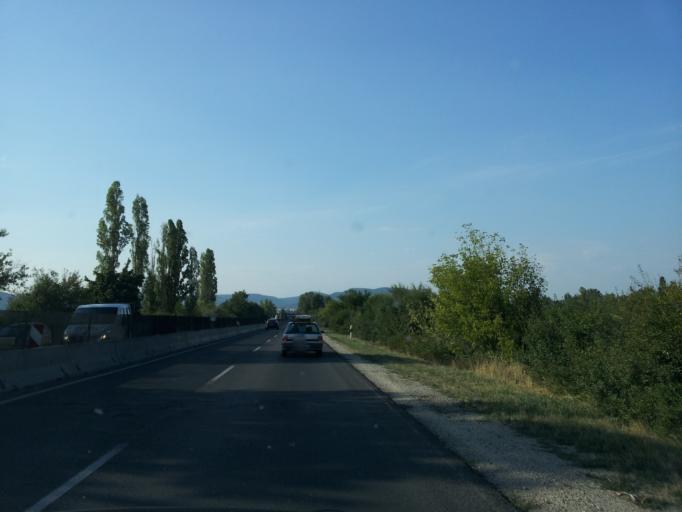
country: HU
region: Pest
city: Budakalasz
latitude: 47.6371
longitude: 19.0697
